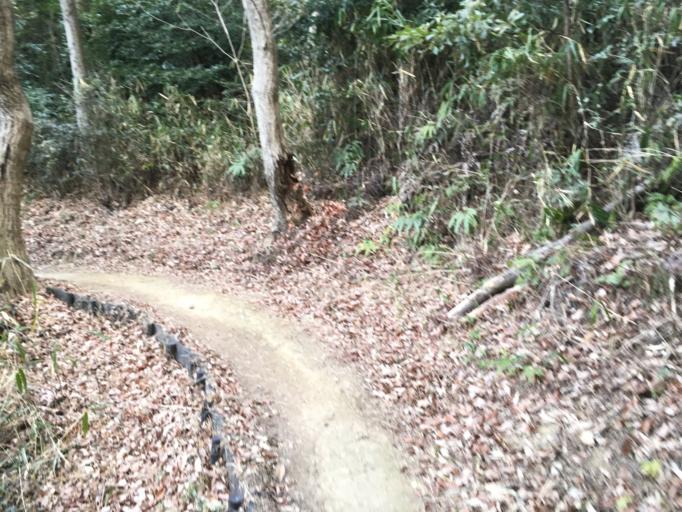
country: JP
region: Aichi
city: Toyohashi
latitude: 34.7353
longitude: 137.4489
